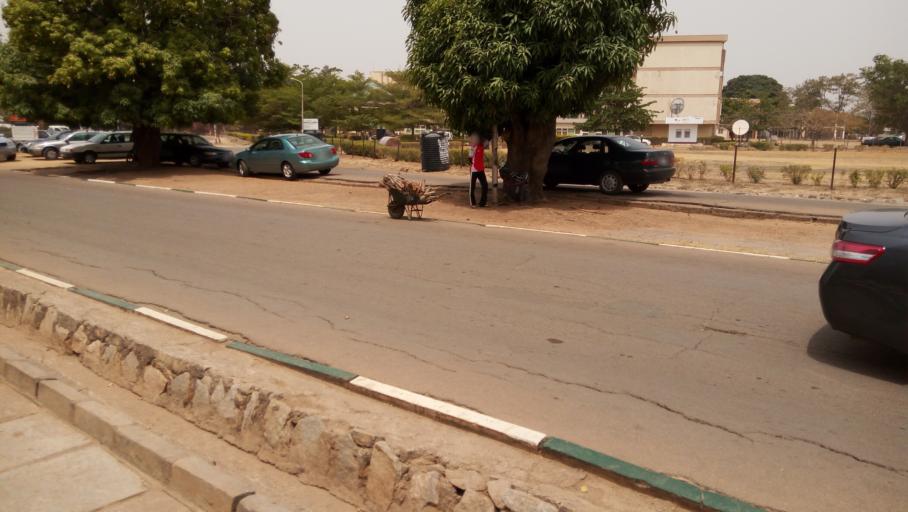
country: NG
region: Kaduna
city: Zaria
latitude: 11.1551
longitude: 7.6515
